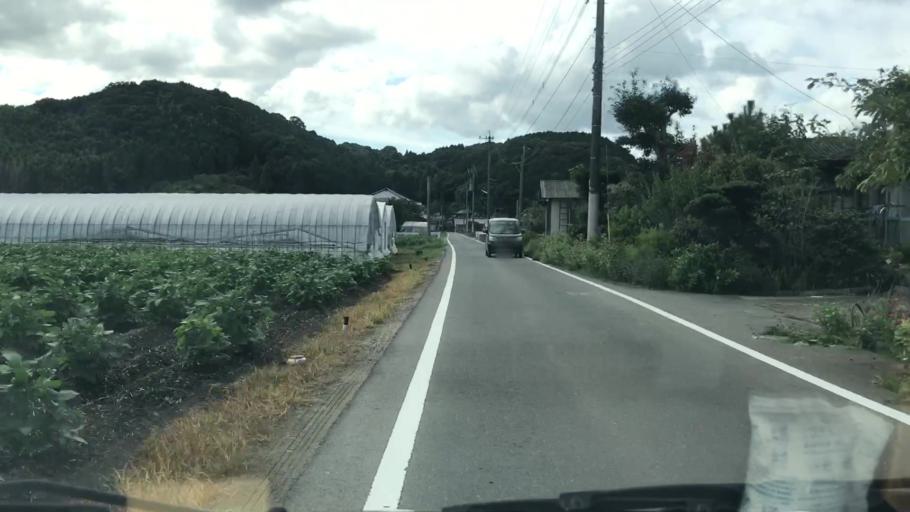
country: JP
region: Saga Prefecture
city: Kashima
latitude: 33.1166
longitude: 130.0738
